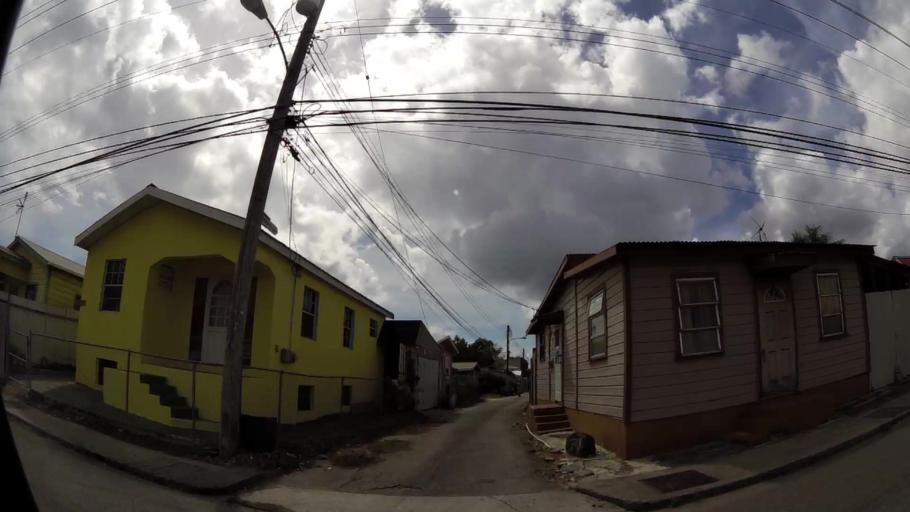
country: BB
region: Saint Michael
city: Bridgetown
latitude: 13.1081
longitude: -59.6215
